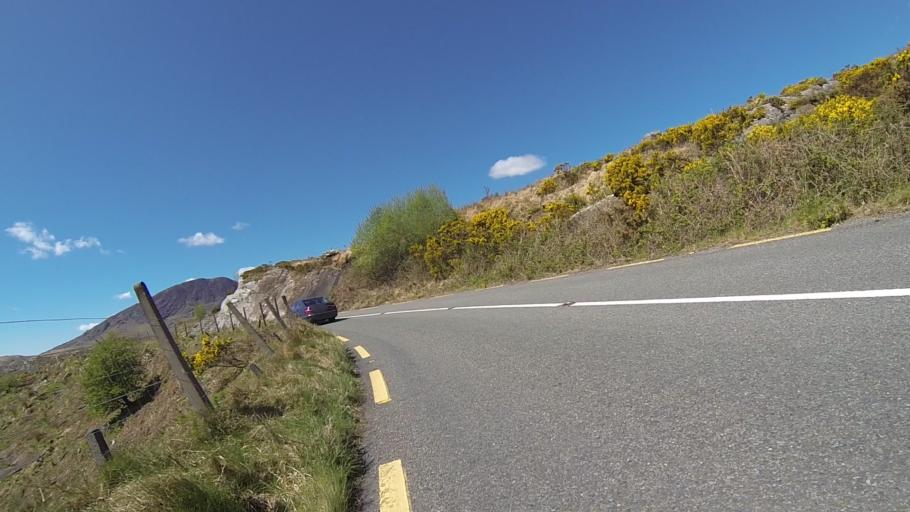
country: IE
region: Munster
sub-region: Ciarrai
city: Kenmare
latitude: 51.9264
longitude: -9.6368
